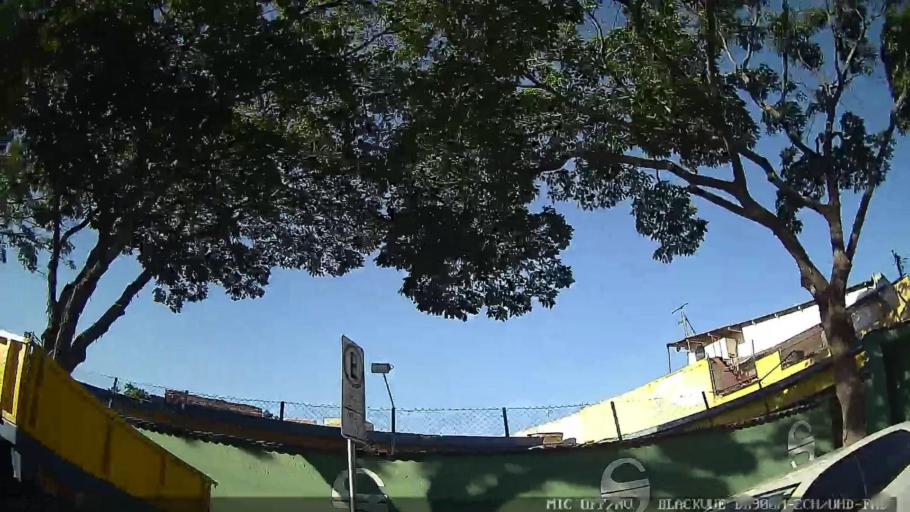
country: BR
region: Sao Paulo
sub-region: Guarulhos
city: Guarulhos
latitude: -23.5306
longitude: -46.5054
